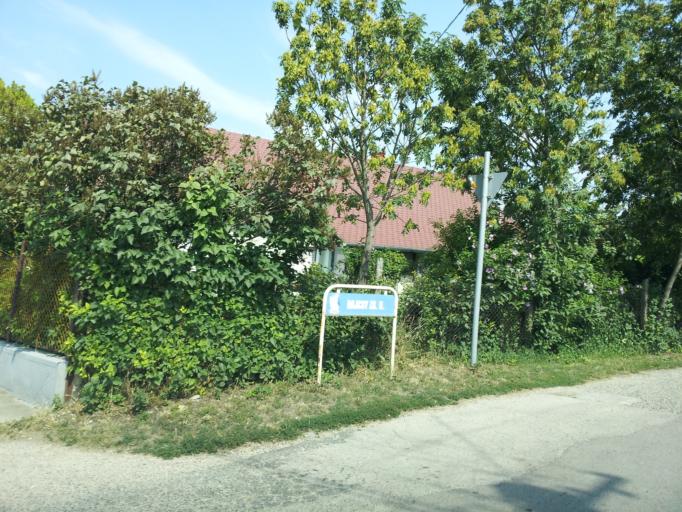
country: HU
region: Veszprem
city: Balatonkenese
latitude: 47.0807
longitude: 18.0796
